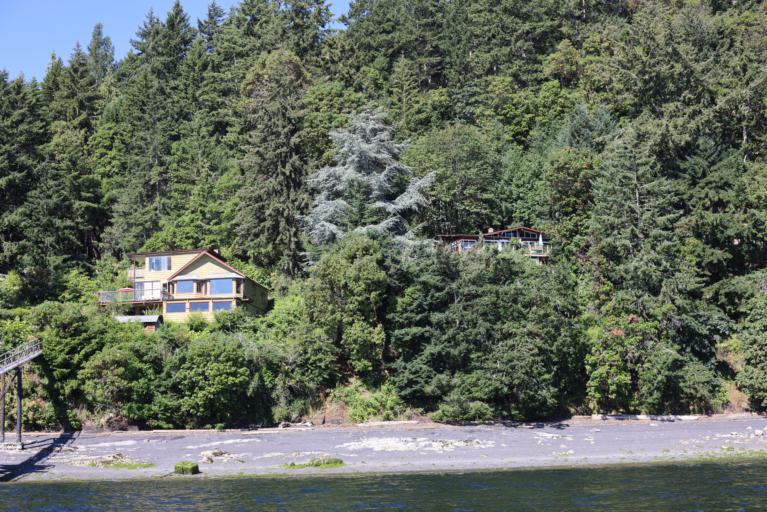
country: CA
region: British Columbia
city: North Cowichan
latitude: 48.8079
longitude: -123.6046
